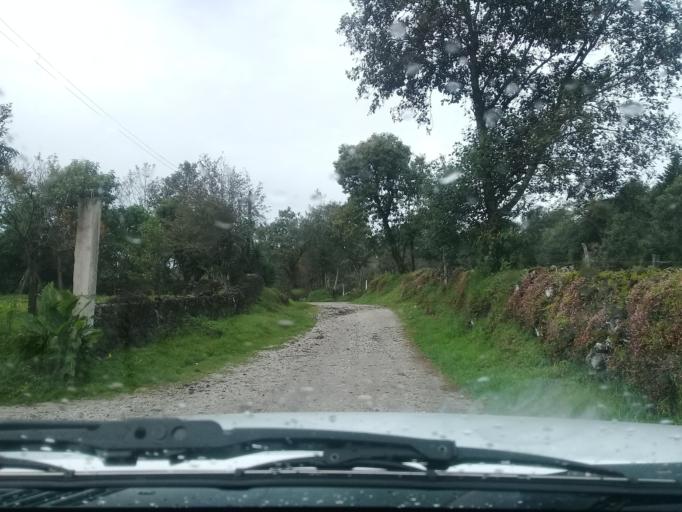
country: MX
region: Veracruz
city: Rafael Lucio
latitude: 19.6210
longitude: -96.9983
